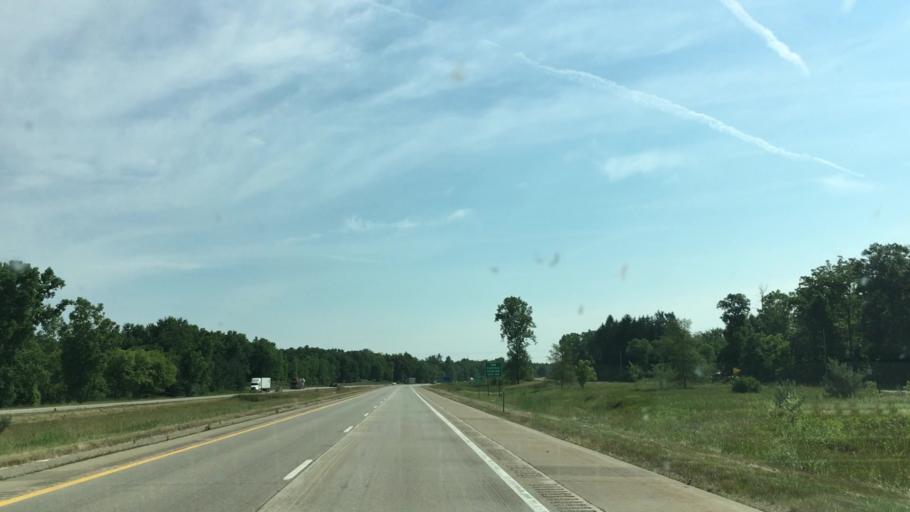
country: US
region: Michigan
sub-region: Ingham County
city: Haslett
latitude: 42.7927
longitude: -84.3693
